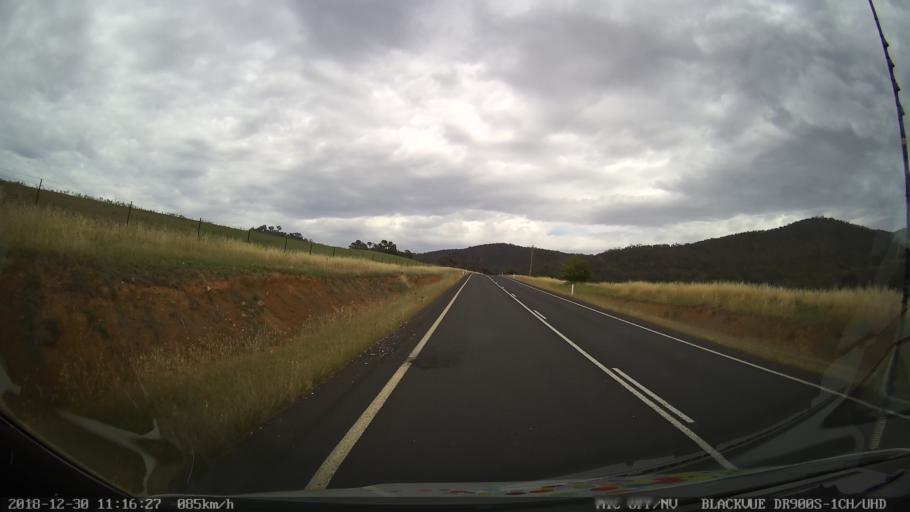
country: AU
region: New South Wales
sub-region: Snowy River
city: Jindabyne
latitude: -36.5408
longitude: 148.7069
